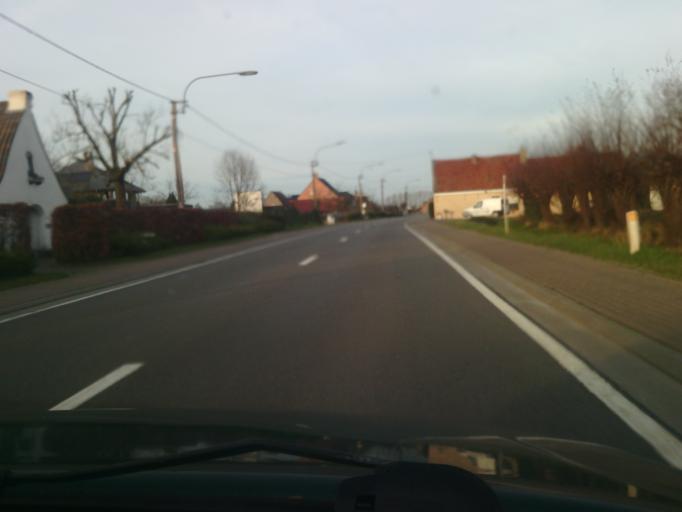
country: BE
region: Flanders
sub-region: Provincie Oost-Vlaanderen
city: Laarne
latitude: 51.0510
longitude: 3.8810
